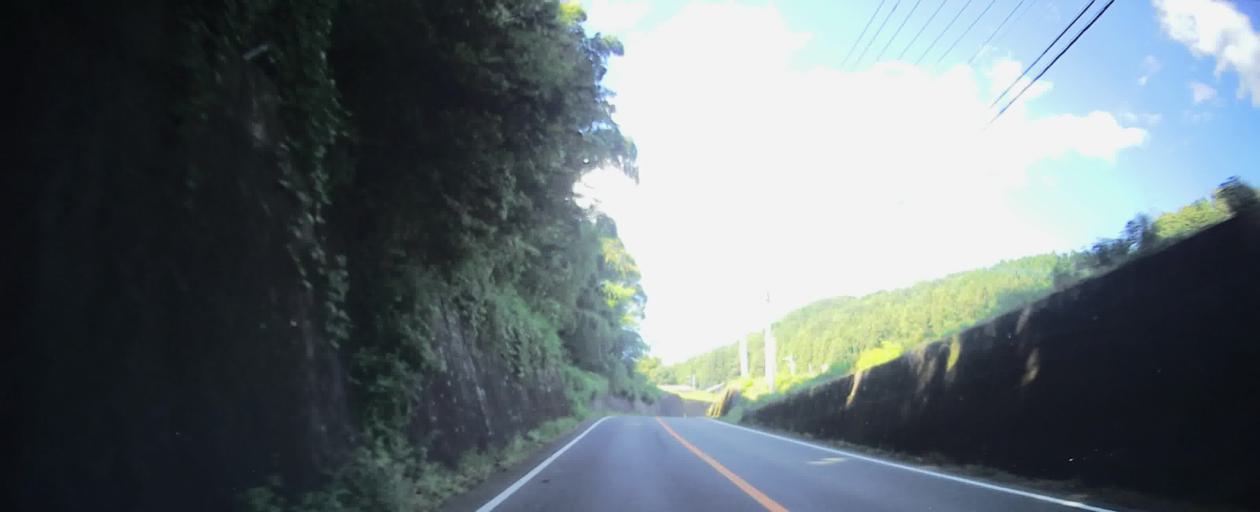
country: JP
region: Gunma
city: Kanekomachi
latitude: 36.4218
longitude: 138.9356
